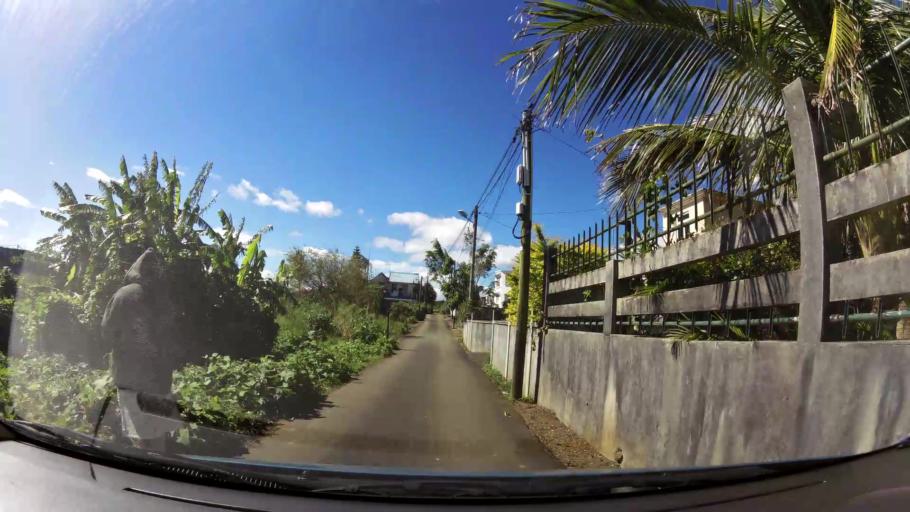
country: MU
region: Plaines Wilhems
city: Curepipe
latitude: -20.3429
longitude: 57.4940
